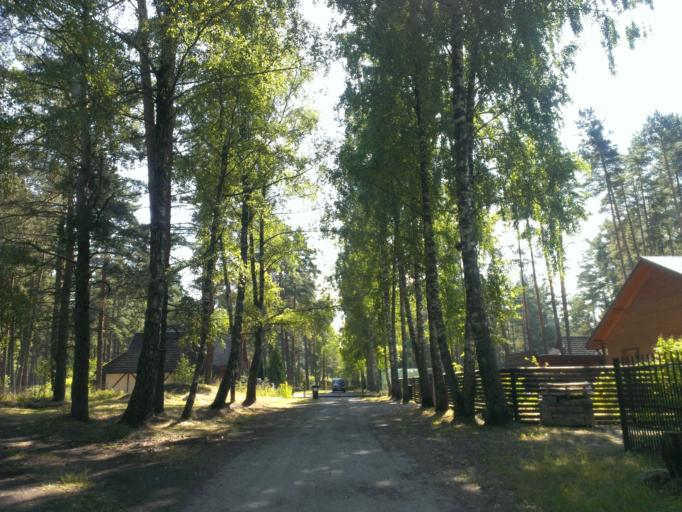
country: LV
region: Adazi
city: Adazi
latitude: 57.1211
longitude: 24.3423
